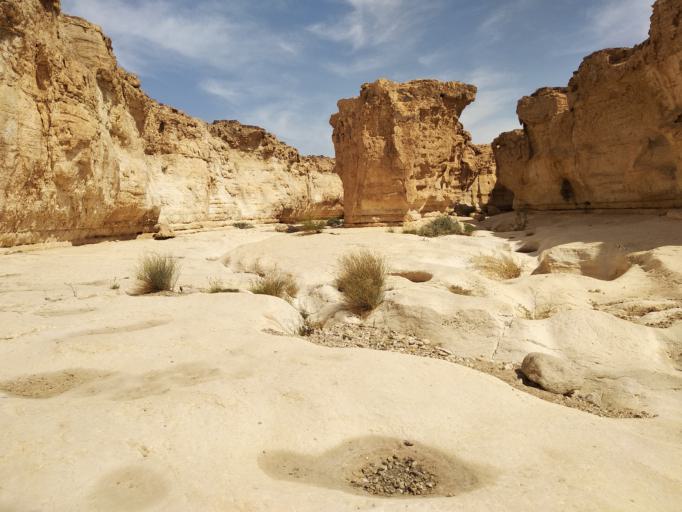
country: JO
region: Karak
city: Safi
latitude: 31.0096
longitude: 35.2886
